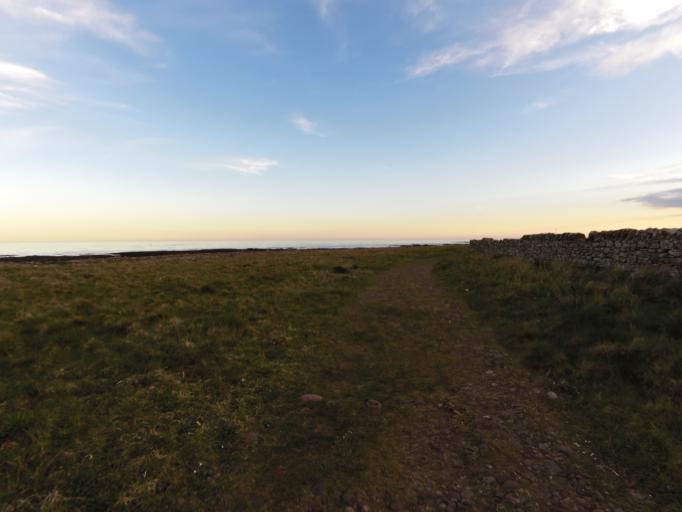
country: GB
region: Scotland
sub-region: Aberdeenshire
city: Inverbervie
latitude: 56.8075
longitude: -2.3085
